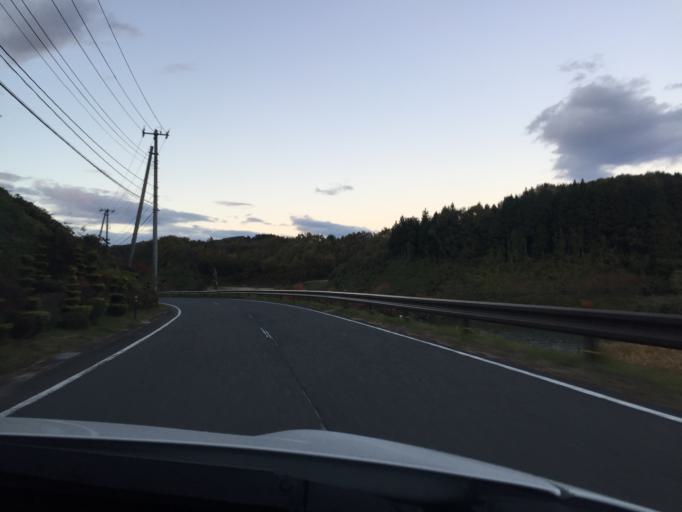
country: JP
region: Fukushima
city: Funehikimachi-funehiki
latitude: 37.2772
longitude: 140.5806
